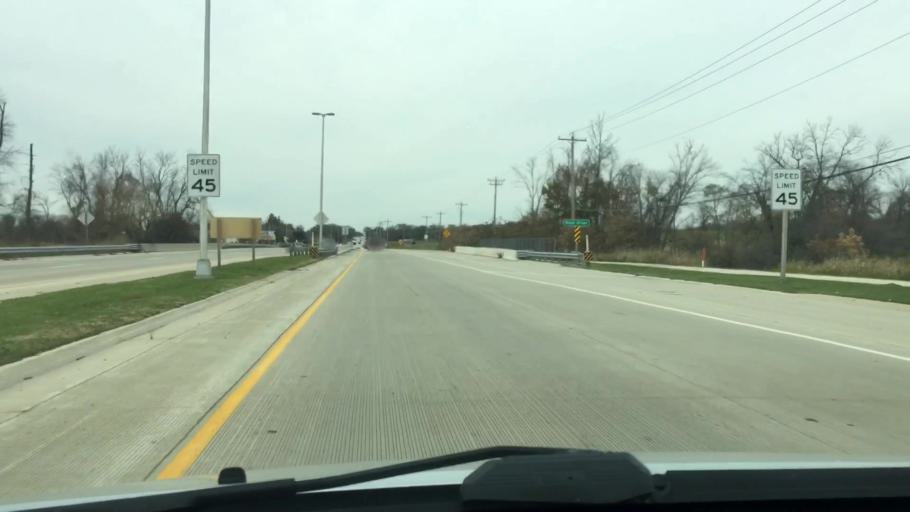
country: US
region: Wisconsin
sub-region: Milwaukee County
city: Franklin
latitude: 42.8727
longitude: -87.9938
